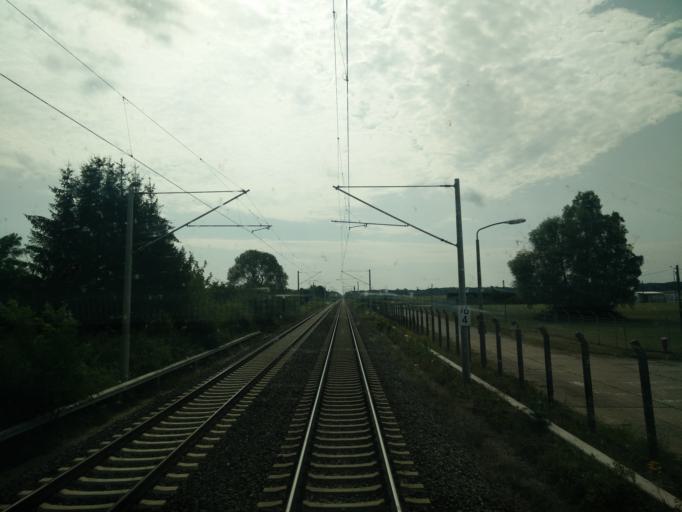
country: DE
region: Brandenburg
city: Luebben
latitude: 51.9273
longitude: 13.8909
